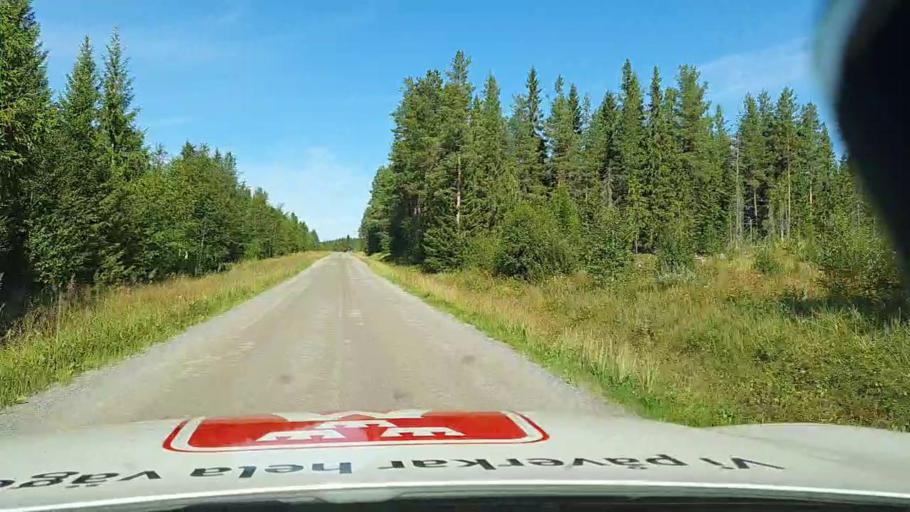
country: SE
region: Jaemtland
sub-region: Stroemsunds Kommun
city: Stroemsund
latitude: 63.6841
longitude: 15.3883
